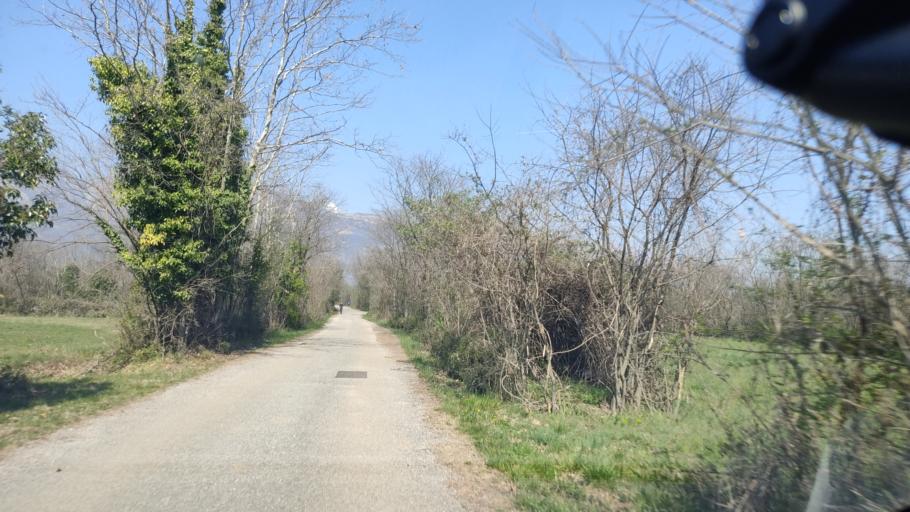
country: IT
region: Friuli Venezia Giulia
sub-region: Provincia di Pordenone
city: Budoia
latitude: 46.0342
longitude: 12.5405
